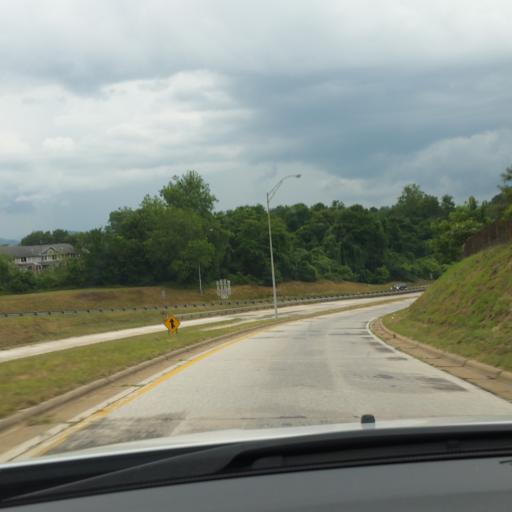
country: US
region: North Carolina
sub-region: Buncombe County
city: Asheville
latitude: 35.5933
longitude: -82.5673
